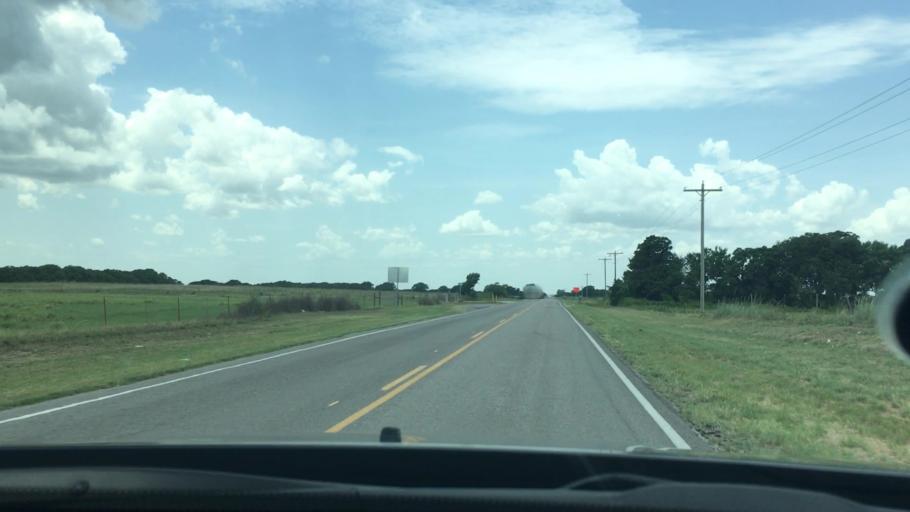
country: US
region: Oklahoma
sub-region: Carter County
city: Wilson
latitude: 33.9404
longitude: -97.4030
